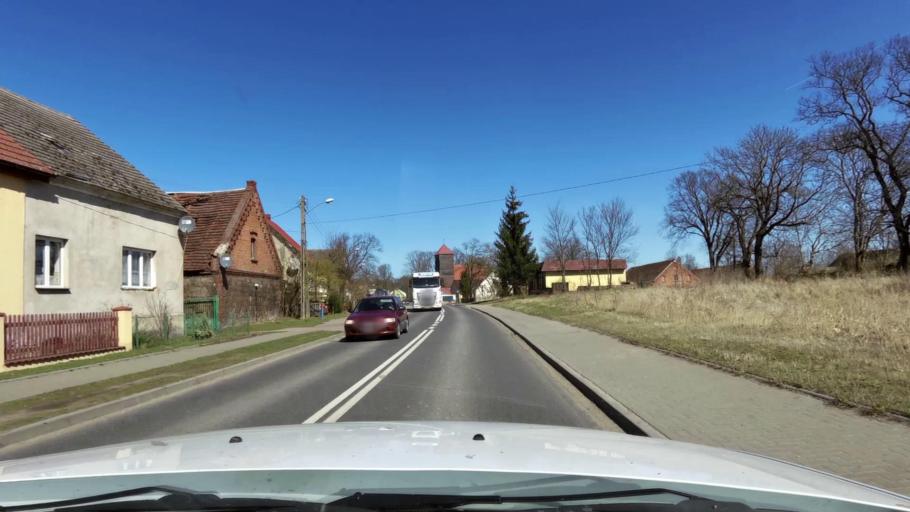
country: PL
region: West Pomeranian Voivodeship
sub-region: Powiat gryfinski
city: Cedynia
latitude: 52.8850
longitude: 14.2857
